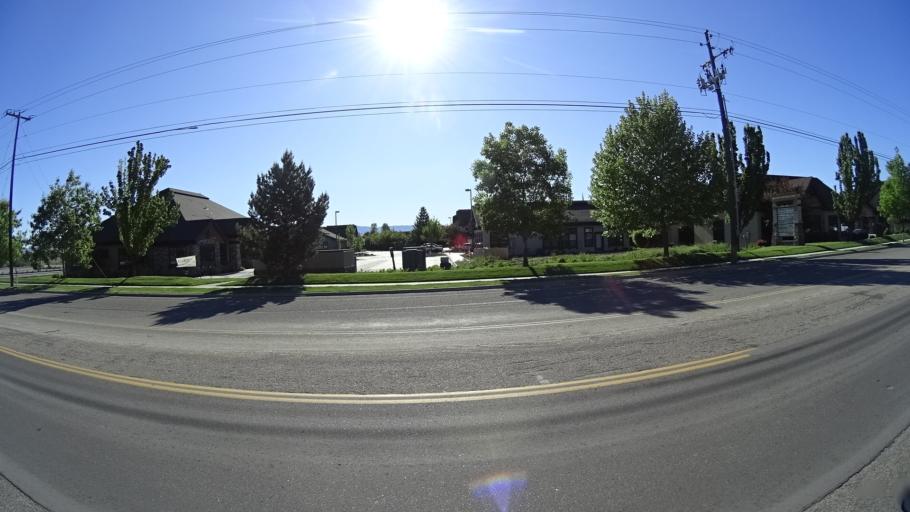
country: US
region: Idaho
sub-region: Ada County
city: Meridian
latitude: 43.6572
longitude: -116.4139
